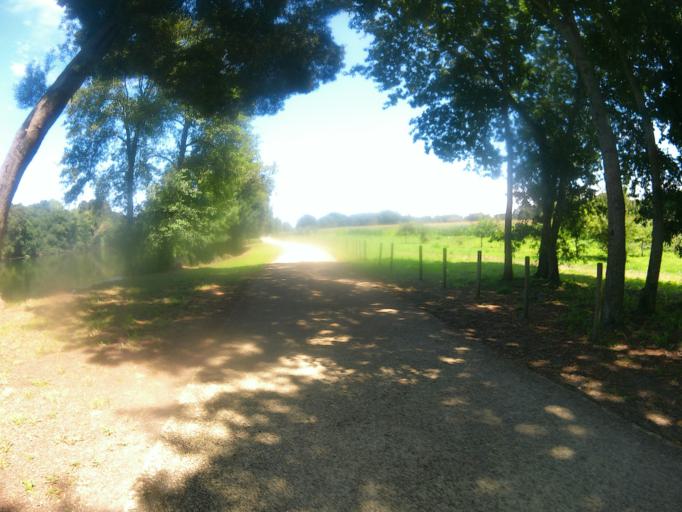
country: PT
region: Viana do Castelo
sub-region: Vila Nova de Cerveira
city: Vila Nova de Cerveira
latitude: 41.9637
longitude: -8.7412
